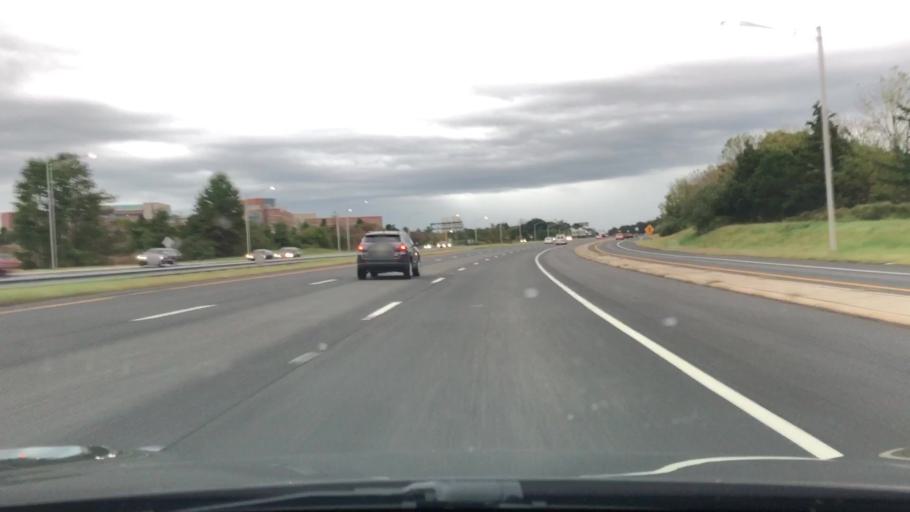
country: US
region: New Jersey
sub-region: Mercer County
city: Ewing
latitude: 40.2894
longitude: -74.8101
